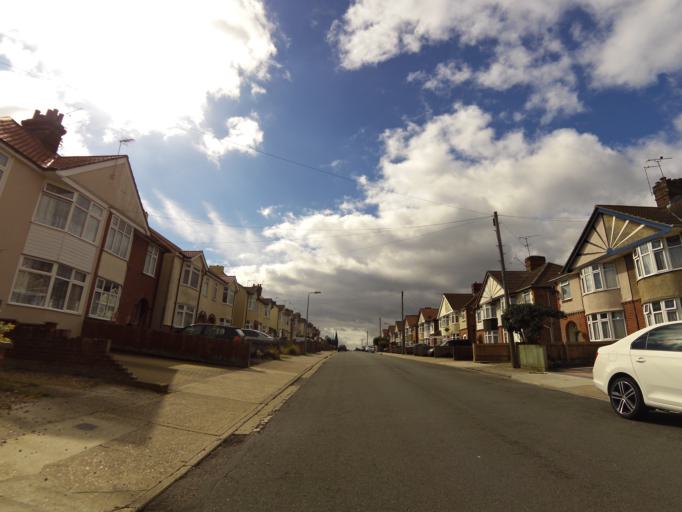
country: GB
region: England
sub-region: Suffolk
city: Ipswich
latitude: 52.0713
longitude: 1.1364
